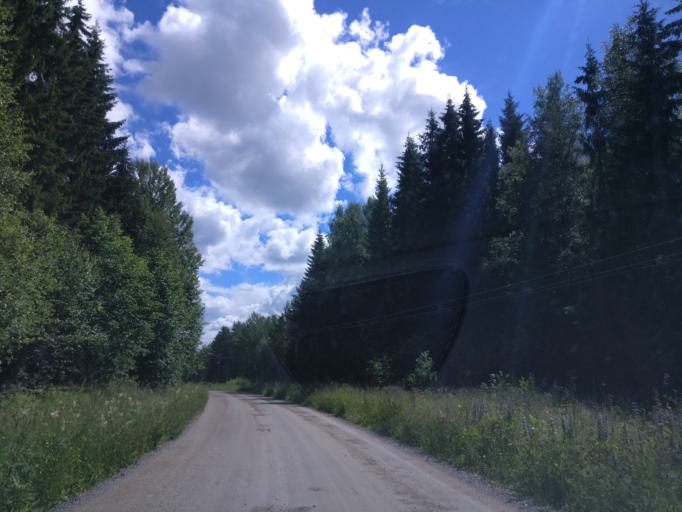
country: SE
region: Vaermland
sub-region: Hagfors Kommun
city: Hagfors
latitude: 60.0302
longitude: 13.6693
